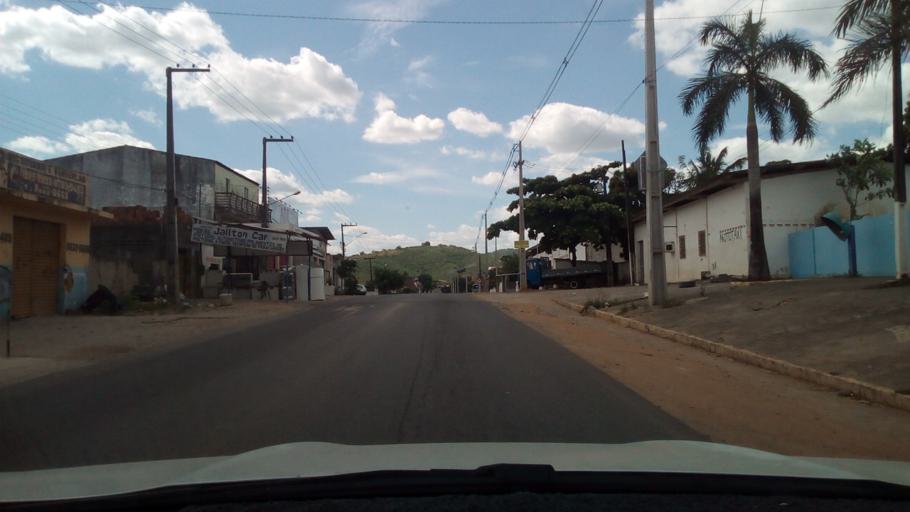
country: BR
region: Paraiba
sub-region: Guarabira
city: Guarabira
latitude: -6.8665
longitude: -35.4911
